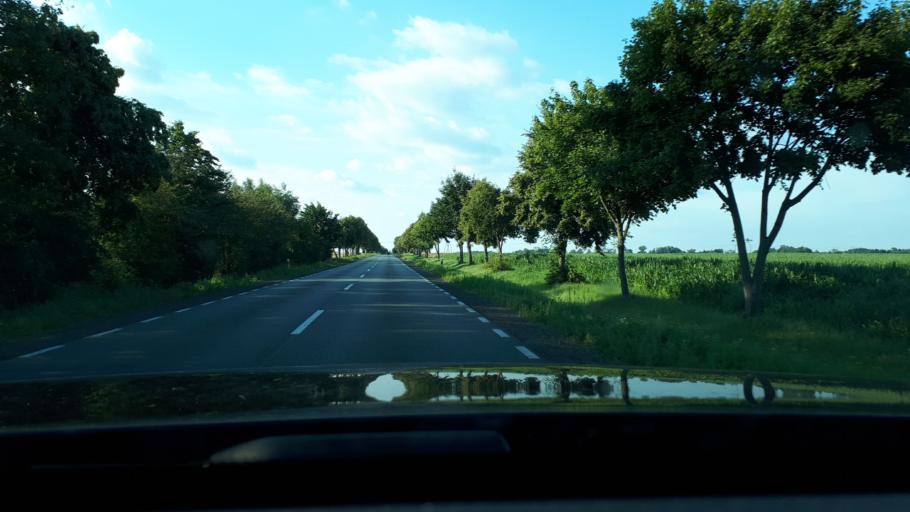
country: PL
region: Masovian Voivodeship
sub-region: Powiat ciechanowski
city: Ciechanow
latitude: 52.8348
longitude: 20.6194
